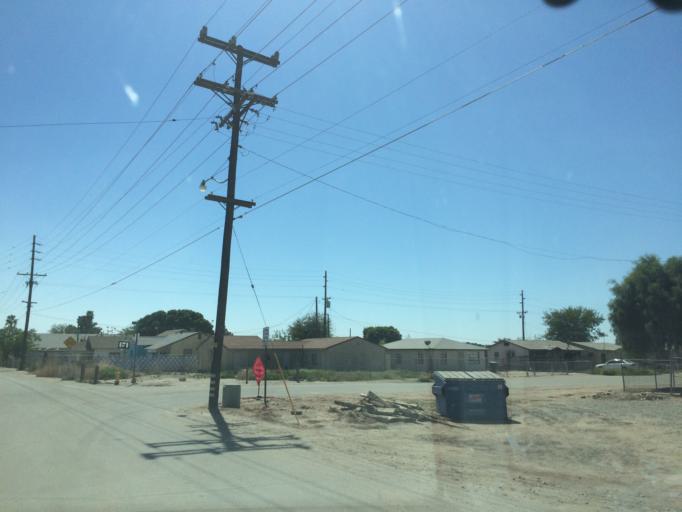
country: US
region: Arizona
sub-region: Yuma County
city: Yuma
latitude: 32.7379
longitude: -114.6332
